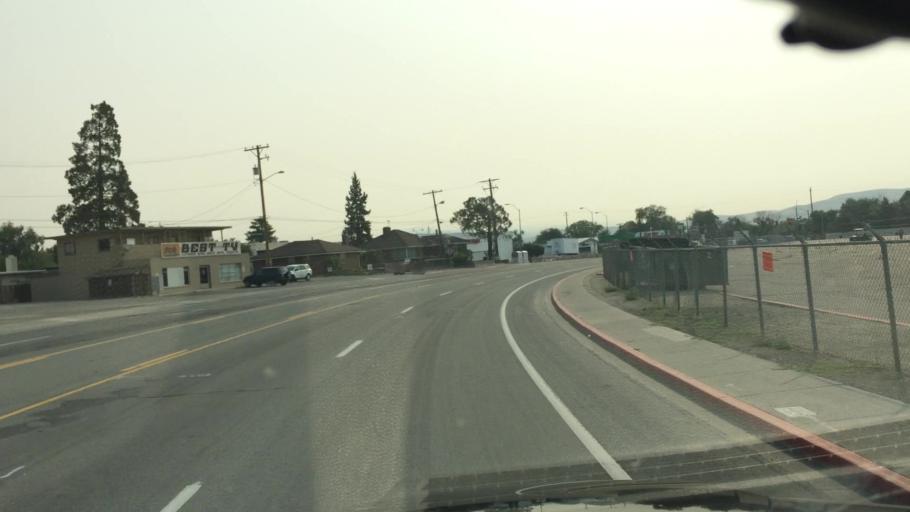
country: US
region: Nevada
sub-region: Washoe County
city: Reno
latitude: 39.5450
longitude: -119.8017
